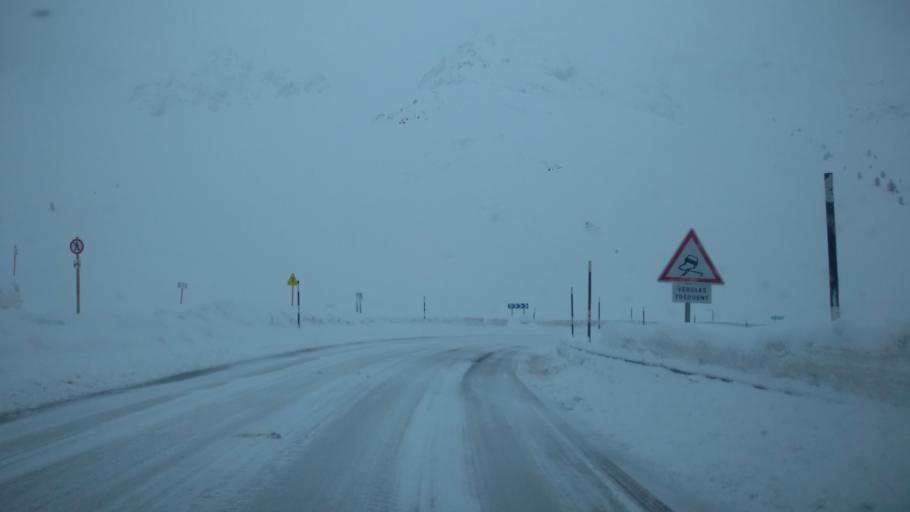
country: FR
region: Provence-Alpes-Cote d'Azur
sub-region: Departement des Hautes-Alpes
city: Le Monetier-les-Bains
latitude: 45.0343
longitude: 6.4053
